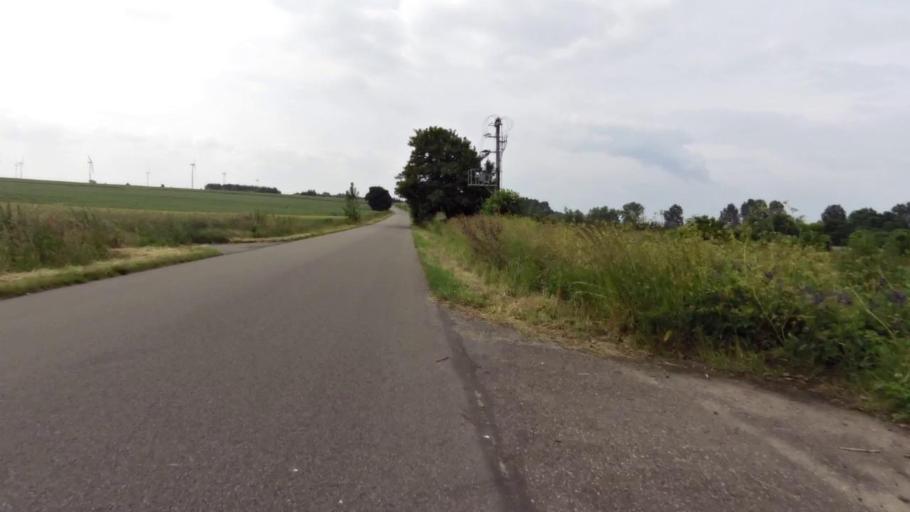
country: PL
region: West Pomeranian Voivodeship
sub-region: Powiat kamienski
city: Wolin
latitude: 53.8171
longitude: 14.6148
